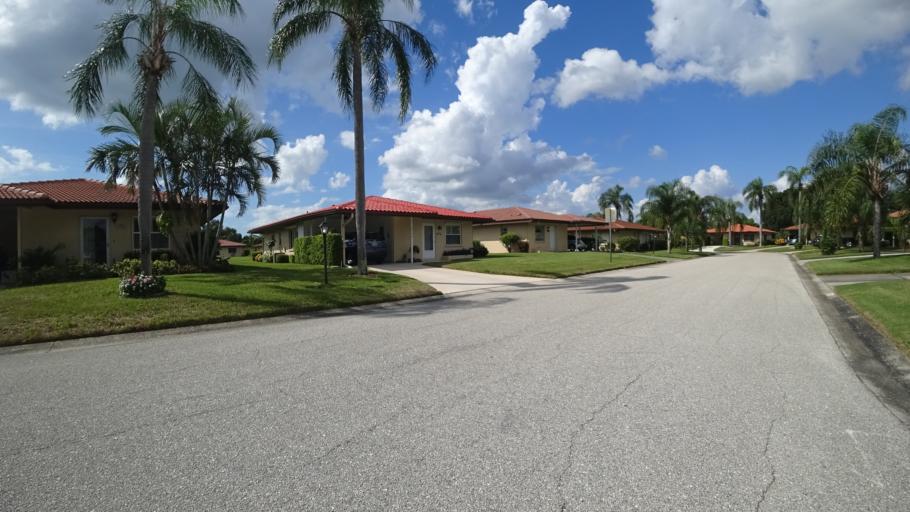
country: US
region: Florida
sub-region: Manatee County
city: Bayshore Gardens
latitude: 27.4274
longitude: -82.5923
